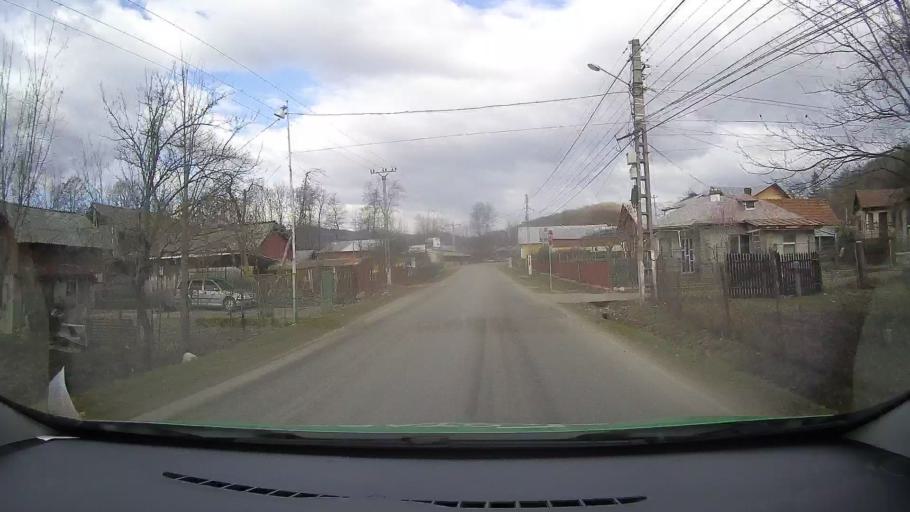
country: RO
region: Prahova
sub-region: Comuna Provita de Jos
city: Provita de Jos
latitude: 45.1270
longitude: 25.6518
